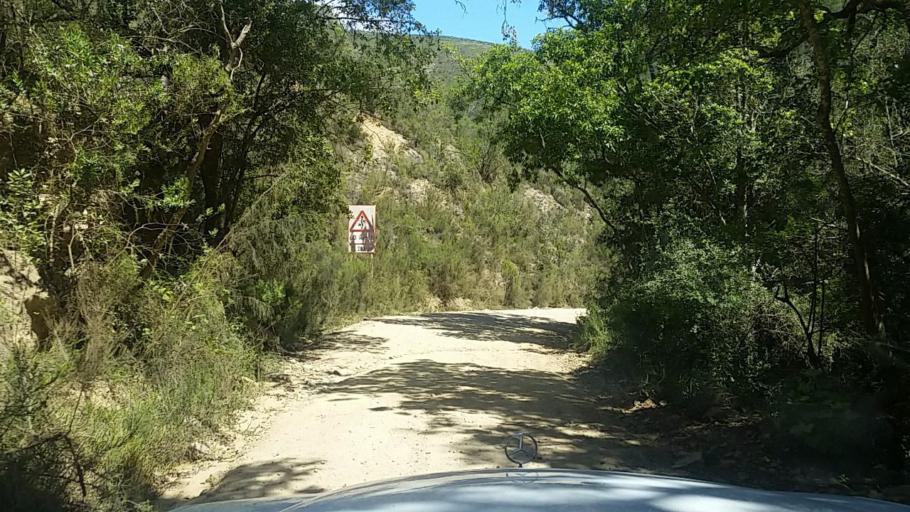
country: ZA
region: Western Cape
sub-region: Eden District Municipality
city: Knysna
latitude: -33.8597
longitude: 23.1759
